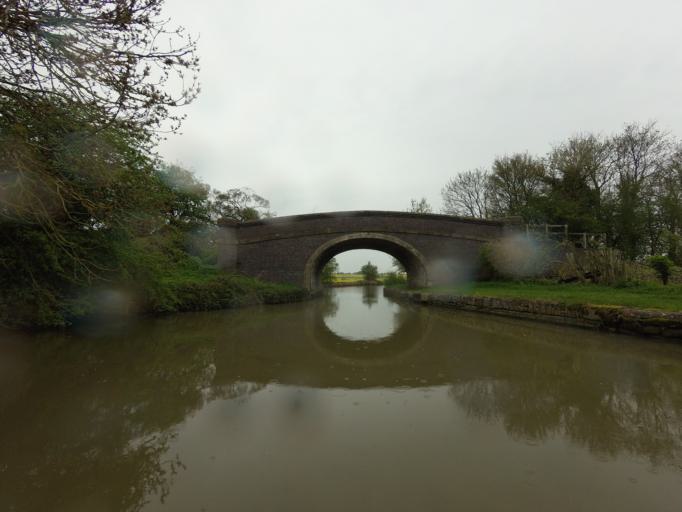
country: GB
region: England
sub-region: Milton Keynes
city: Castlethorpe
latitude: 52.1049
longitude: -0.8864
